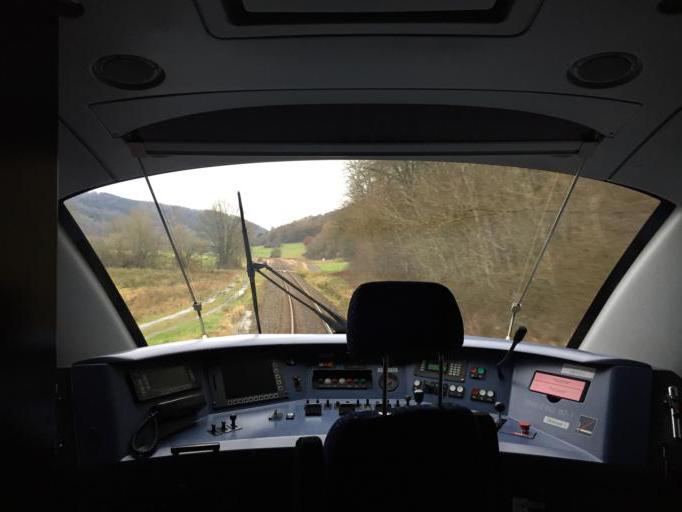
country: DE
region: Hesse
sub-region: Regierungsbezirk Kassel
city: Frankenau
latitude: 51.1480
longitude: 8.8843
